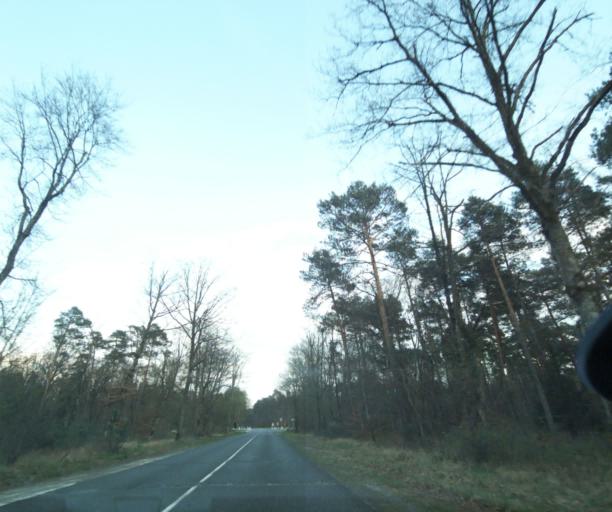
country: FR
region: Ile-de-France
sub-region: Departement de Seine-et-Marne
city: Avon
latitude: 48.3773
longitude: 2.7380
